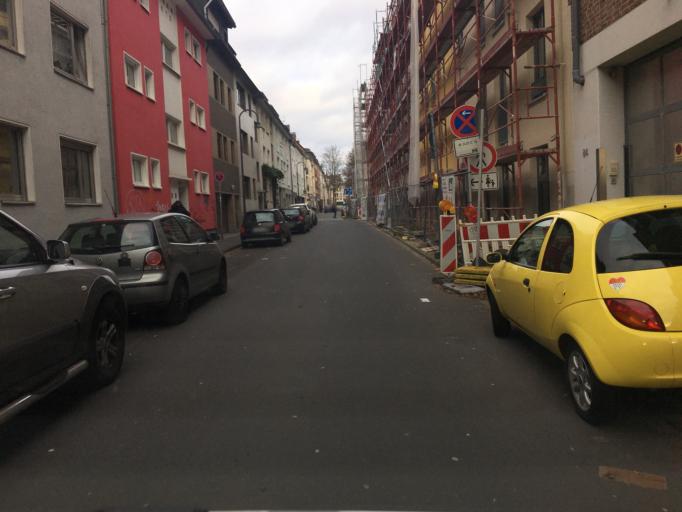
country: DE
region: North Rhine-Westphalia
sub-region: Regierungsbezirk Koln
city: Muelheim
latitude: 50.9644
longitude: 7.0012
